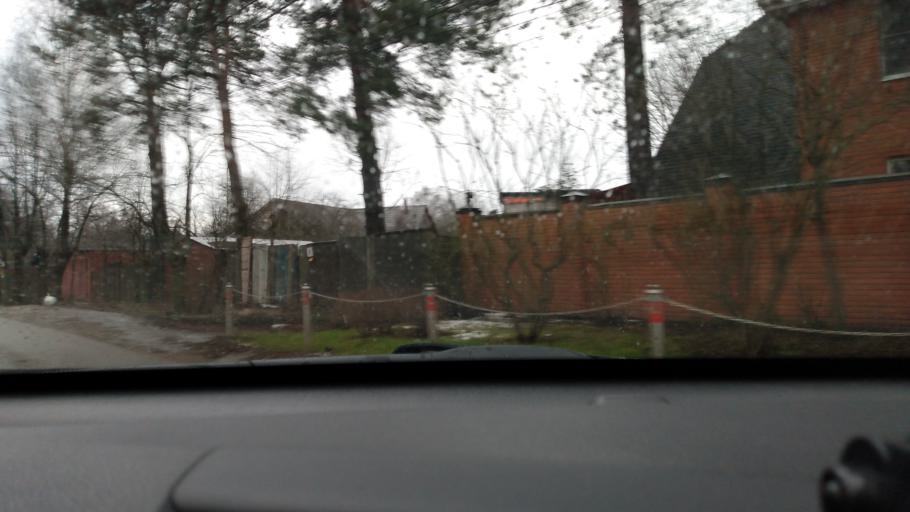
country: RU
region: Moskovskaya
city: Druzhba
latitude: 55.9005
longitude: 37.7474
